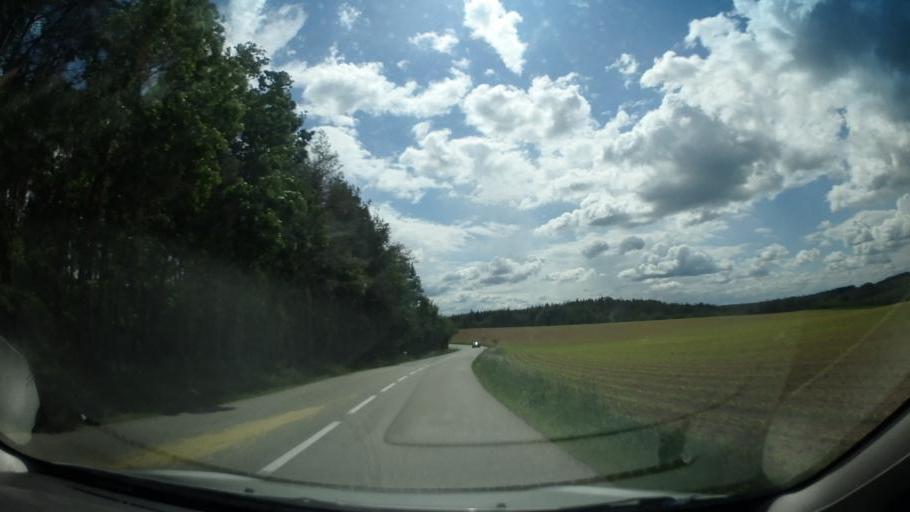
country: CZ
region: South Moravian
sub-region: Okres Blansko
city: Letovice
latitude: 49.5857
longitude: 16.5932
